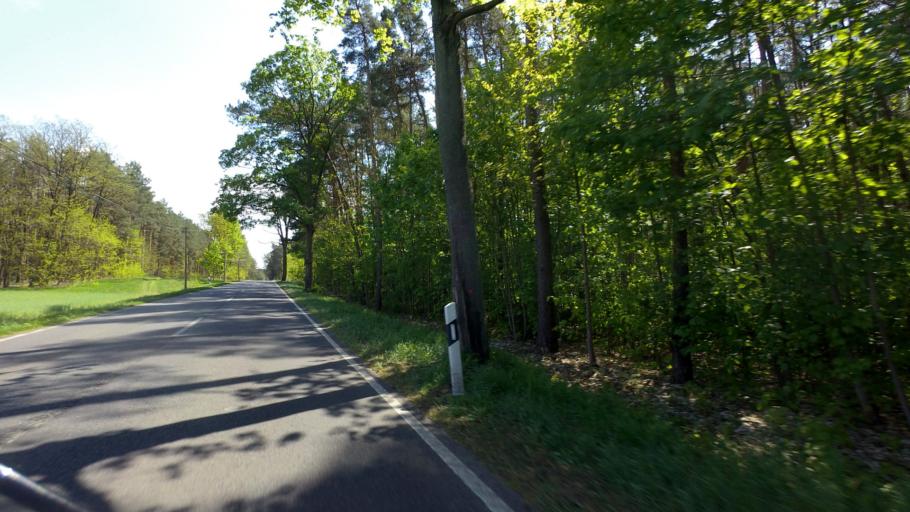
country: DE
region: Brandenburg
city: Lieberose
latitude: 52.0045
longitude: 14.1947
